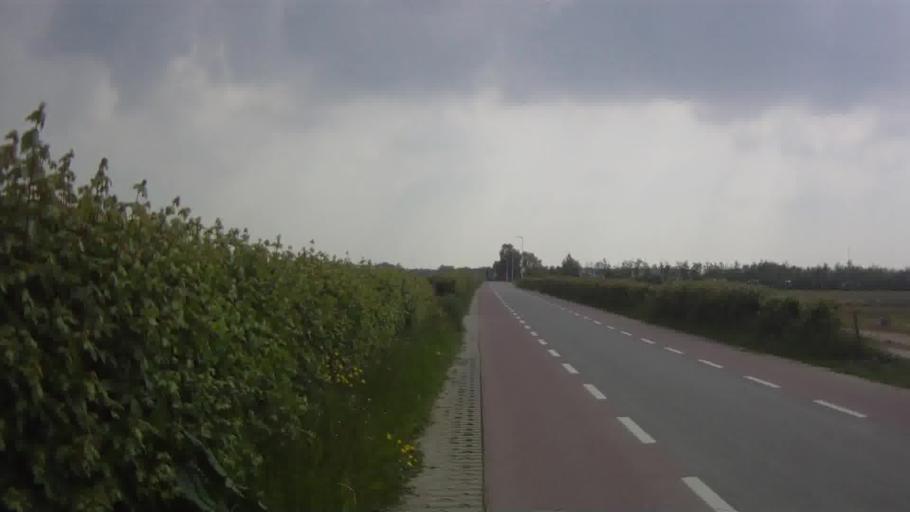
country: NL
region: Utrecht
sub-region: Gemeente Bunnik
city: Bunnik
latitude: 52.0497
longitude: 5.1918
